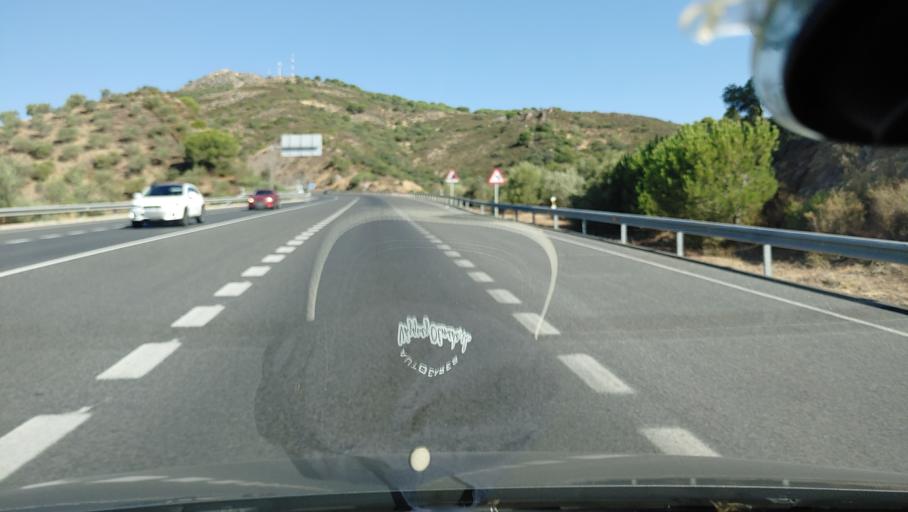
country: ES
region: Andalusia
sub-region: Province of Cordoba
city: Cordoba
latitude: 37.9756
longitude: -4.7715
